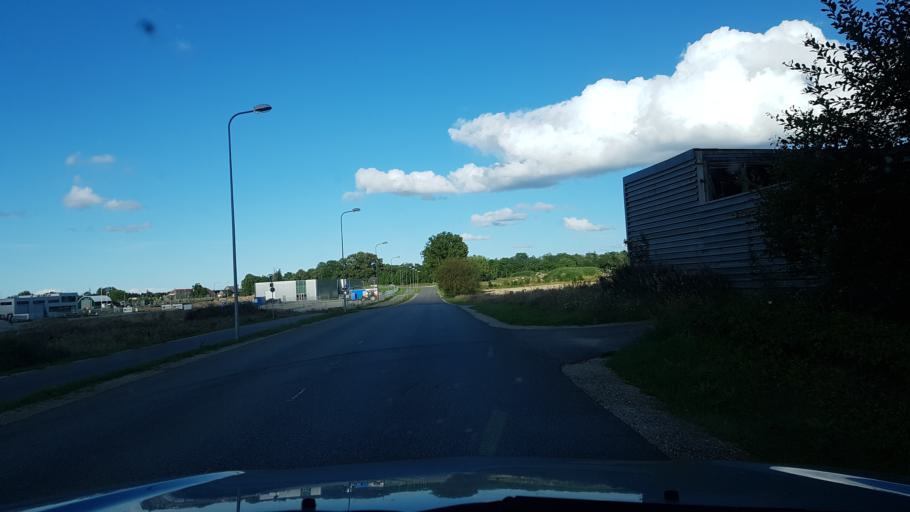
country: EE
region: Harju
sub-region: Kiili vald
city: Kiili
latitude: 59.3347
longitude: 24.8348
